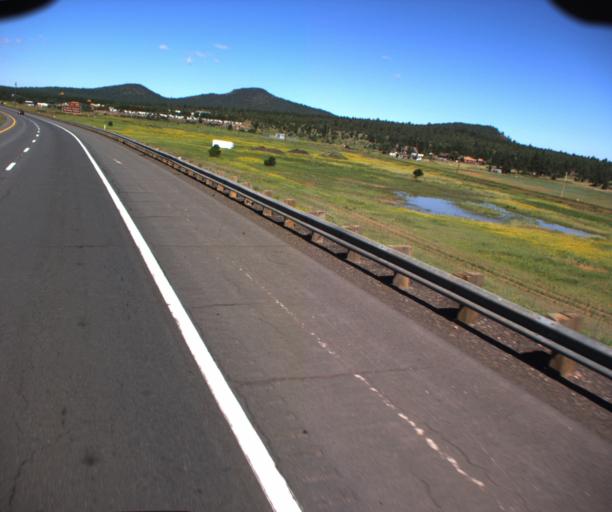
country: US
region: Arizona
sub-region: Coconino County
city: Williams
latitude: 35.2640
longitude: -112.1810
